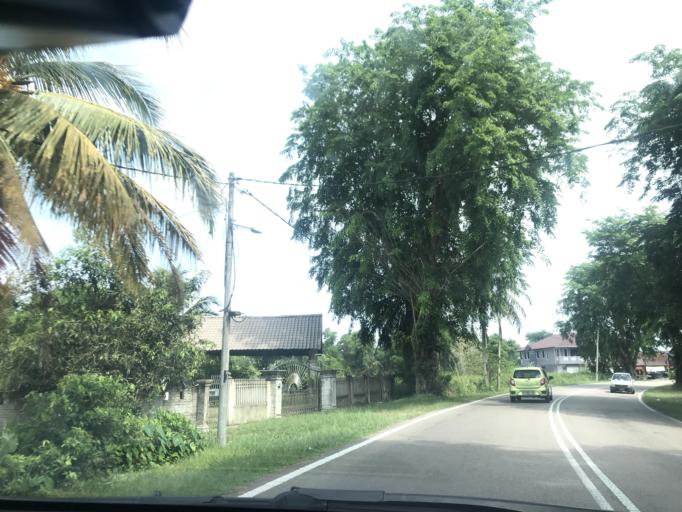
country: MY
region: Kelantan
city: Tumpat
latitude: 6.2014
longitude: 102.1506
